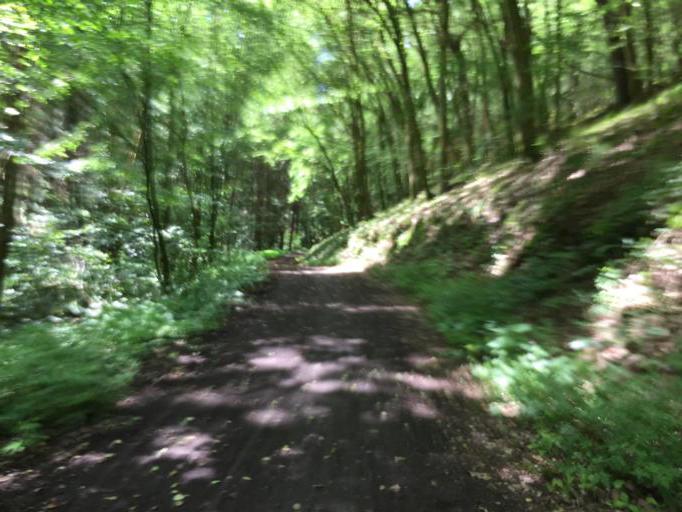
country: DE
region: Rheinland-Pfalz
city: Heilberscheid
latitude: 50.4333
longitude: 7.8775
